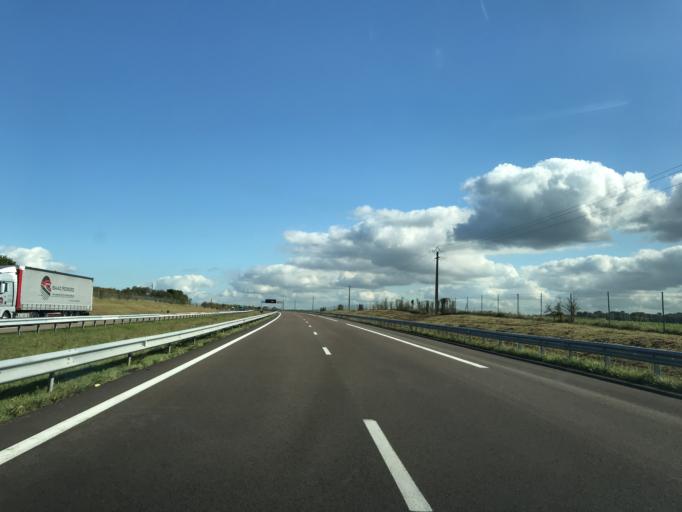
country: FR
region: Ile-de-France
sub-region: Departement de Seine-et-Marne
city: Egreville
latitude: 48.1366
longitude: 2.9214
